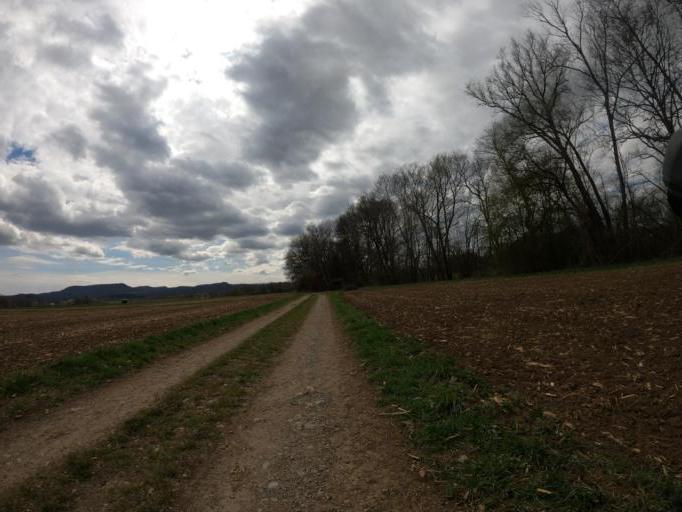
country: DE
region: Baden-Wuerttemberg
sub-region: Tuebingen Region
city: Dusslingen
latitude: 48.4583
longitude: 9.0720
